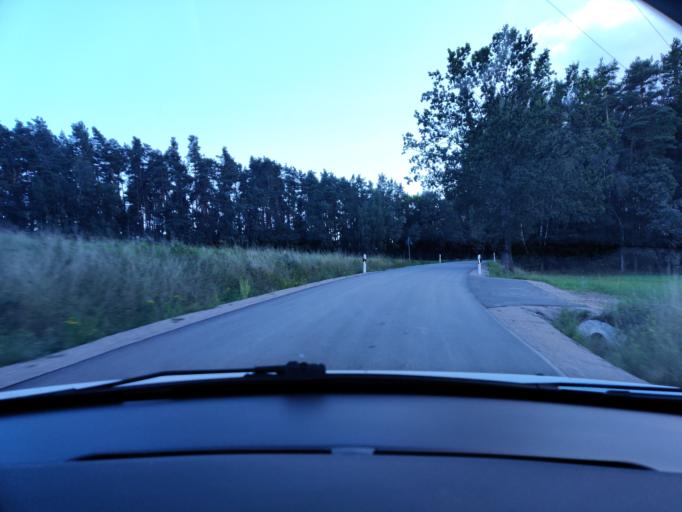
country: DE
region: Bavaria
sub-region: Upper Palatinate
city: Pfreimd
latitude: 49.4841
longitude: 12.1543
